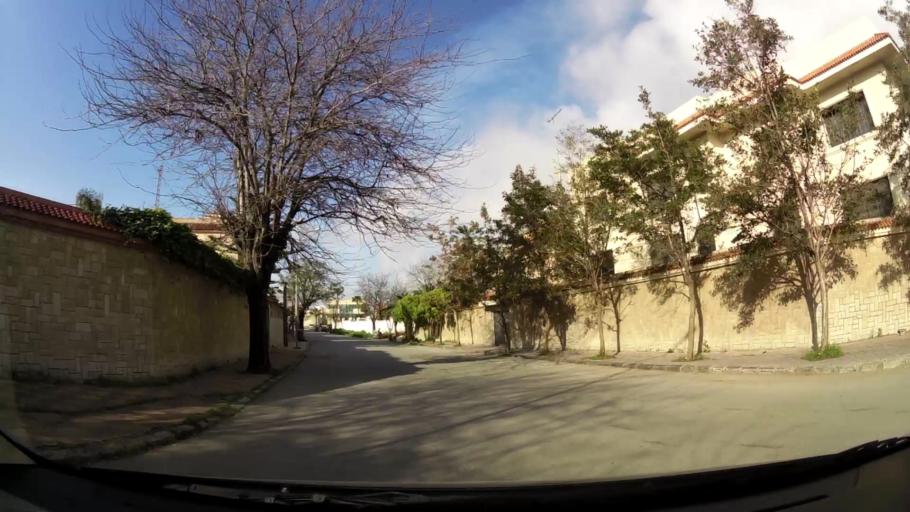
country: MA
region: Tanger-Tetouan
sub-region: Tanger-Assilah
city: Tangier
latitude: 35.7690
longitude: -5.8000
